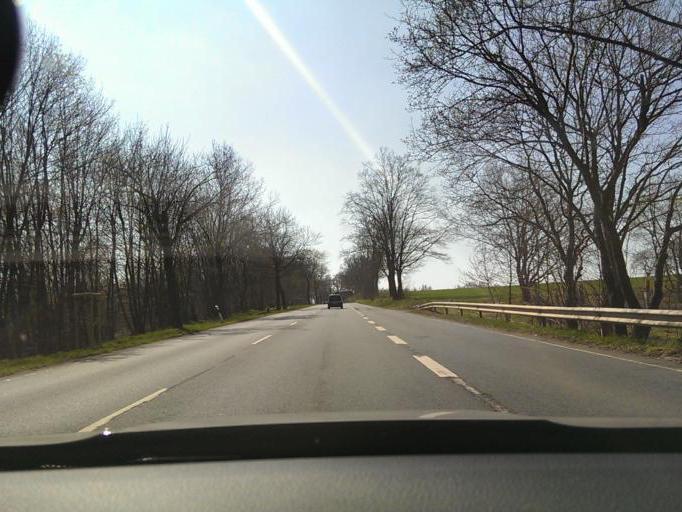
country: DE
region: Lower Saxony
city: Elze
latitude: 52.5553
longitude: 9.7239
